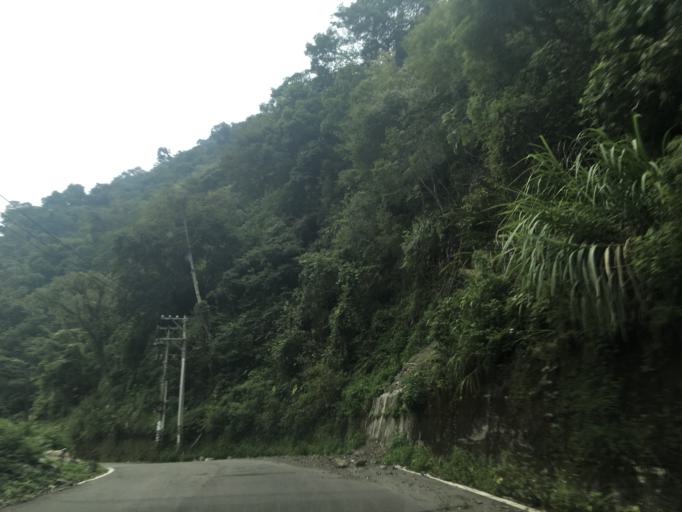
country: TW
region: Taiwan
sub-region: Miaoli
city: Miaoli
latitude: 24.3554
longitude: 120.9492
